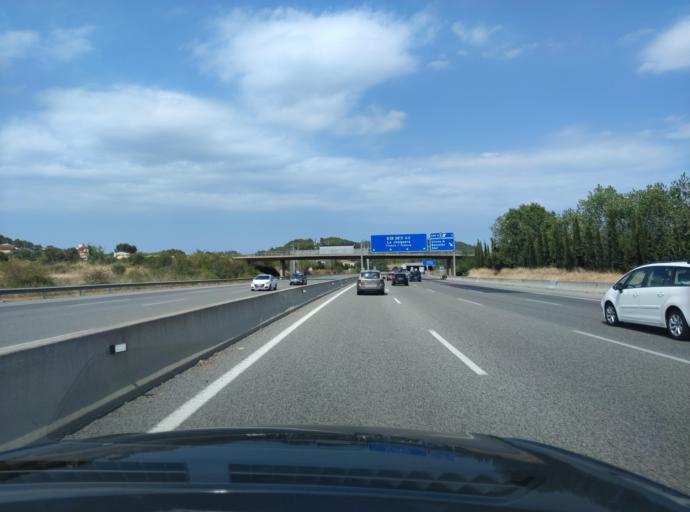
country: ES
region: Catalonia
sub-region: Provincia de Girona
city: Sarria de Ter
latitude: 42.0236
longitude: 2.8182
